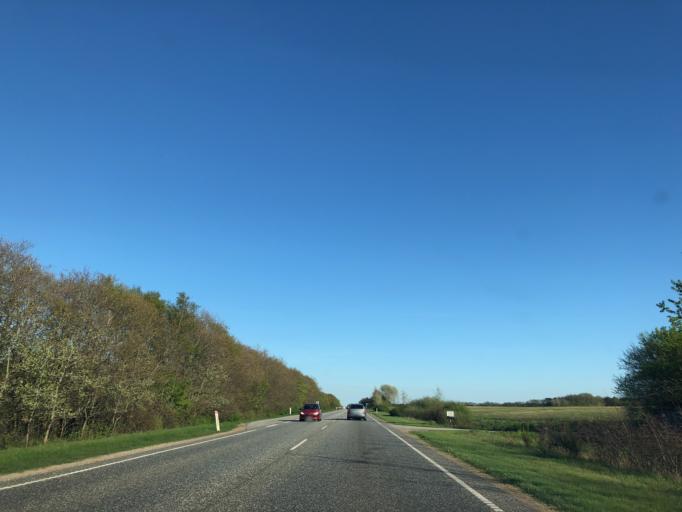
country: DK
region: Central Jutland
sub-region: Herning Kommune
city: Avlum
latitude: 56.3018
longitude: 8.7125
